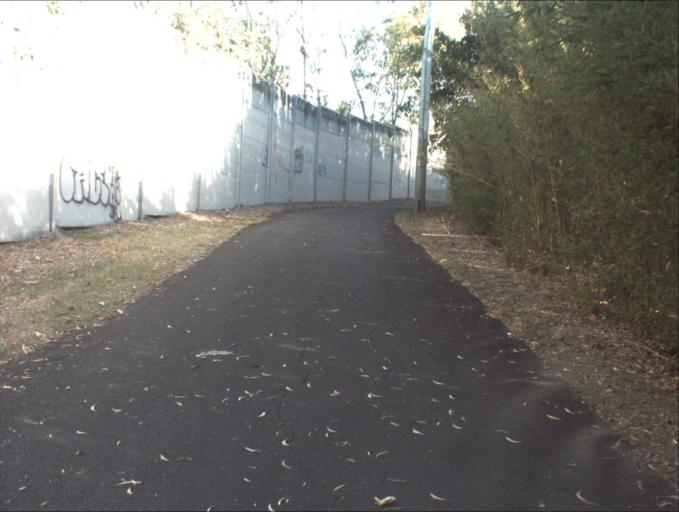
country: AU
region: Queensland
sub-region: Logan
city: Slacks Creek
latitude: -27.6749
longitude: 153.1828
